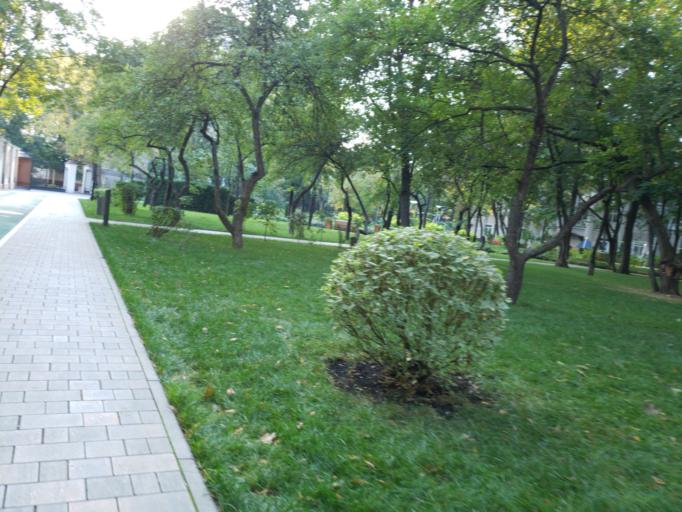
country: RU
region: Moscow
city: Mar'ina Roshcha
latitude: 55.7767
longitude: 37.6114
